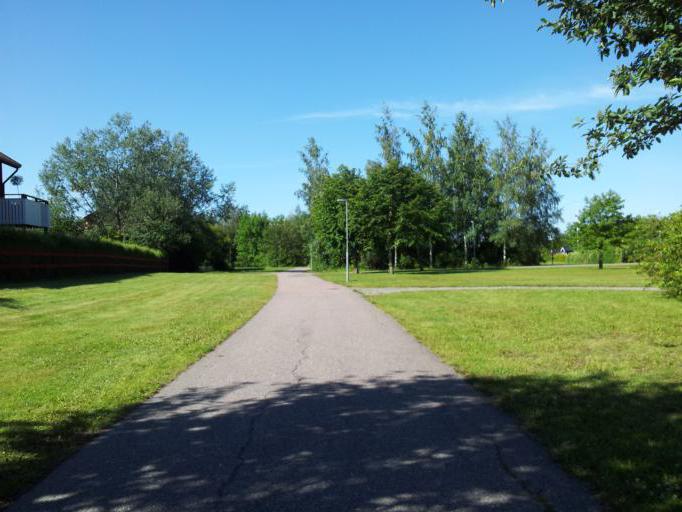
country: SE
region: Uppsala
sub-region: Uppsala Kommun
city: Saevja
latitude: 59.8629
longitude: 17.7055
